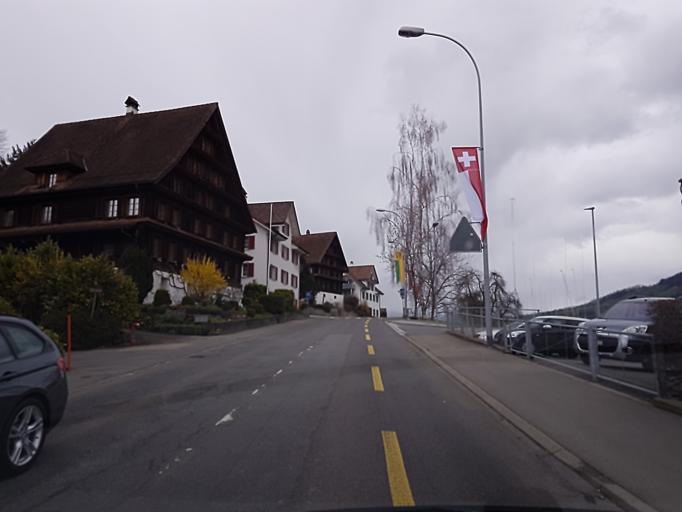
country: CH
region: Lucerne
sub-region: Lucerne-Land District
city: Udligenswil
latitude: 47.0662
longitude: 8.4089
